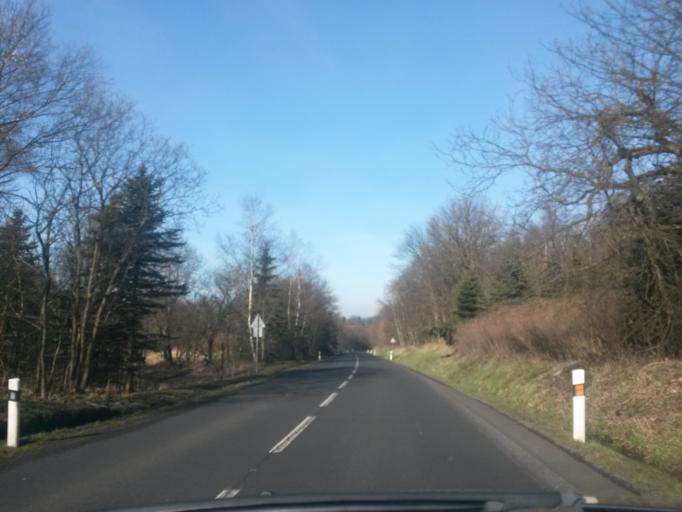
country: CZ
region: Ustecky
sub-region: Okres Chomutov
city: Klasterec nad Ohri
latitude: 50.4538
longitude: 13.1604
